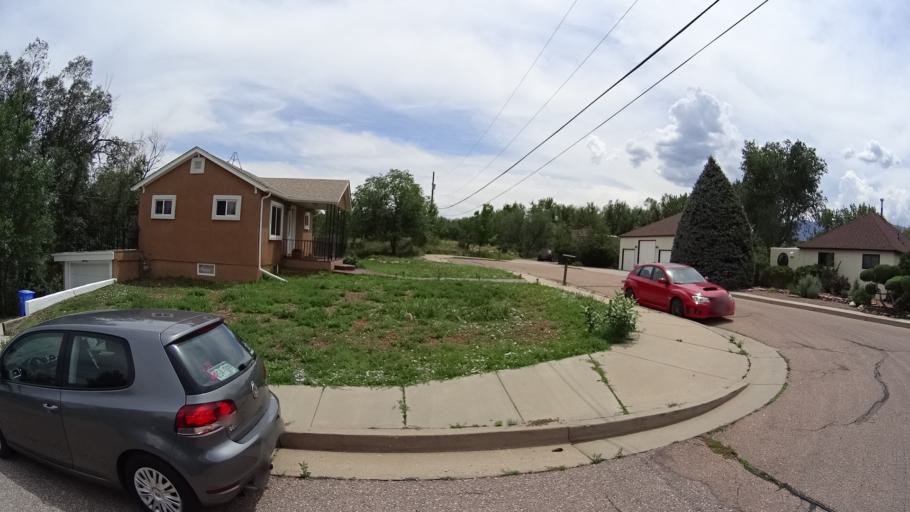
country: US
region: Colorado
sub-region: El Paso County
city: Colorado Springs
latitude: 38.8582
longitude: -104.8373
